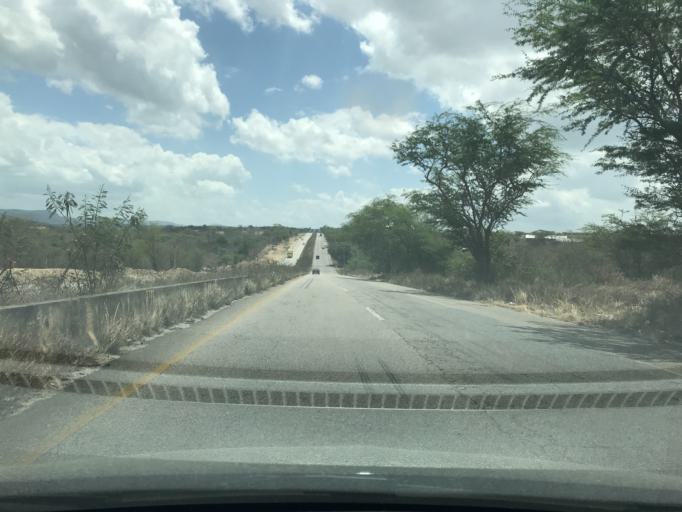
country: BR
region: Pernambuco
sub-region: Caruaru
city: Caruaru
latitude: -8.2998
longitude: -35.9092
